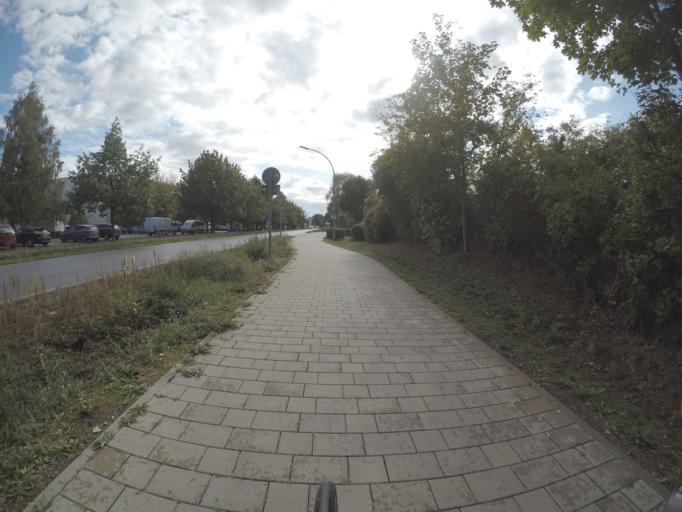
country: DE
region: Brandenburg
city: Strausberg
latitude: 52.5520
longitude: 13.8645
